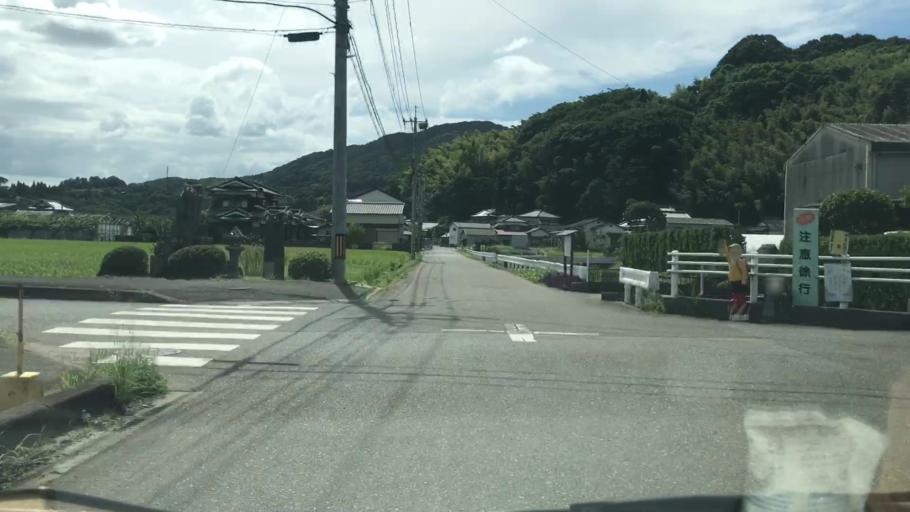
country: JP
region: Saga Prefecture
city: Saga-shi
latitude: 33.2364
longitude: 130.1791
